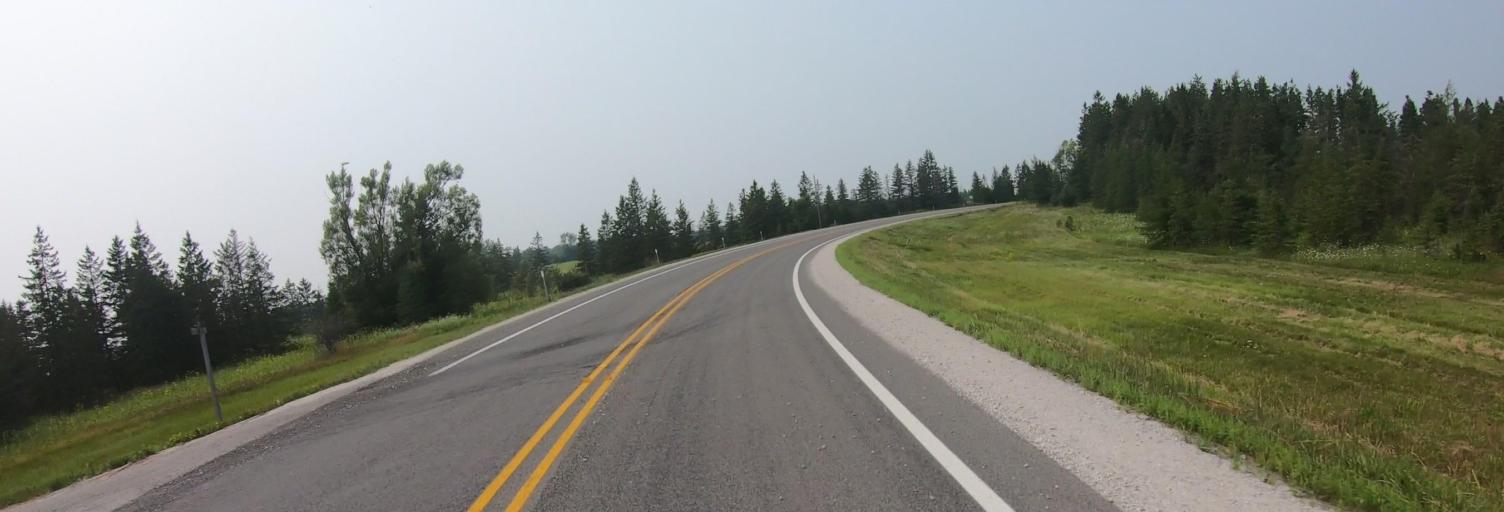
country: US
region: Michigan
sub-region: Chippewa County
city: Sault Ste. Marie
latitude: 46.0720
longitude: -84.2379
